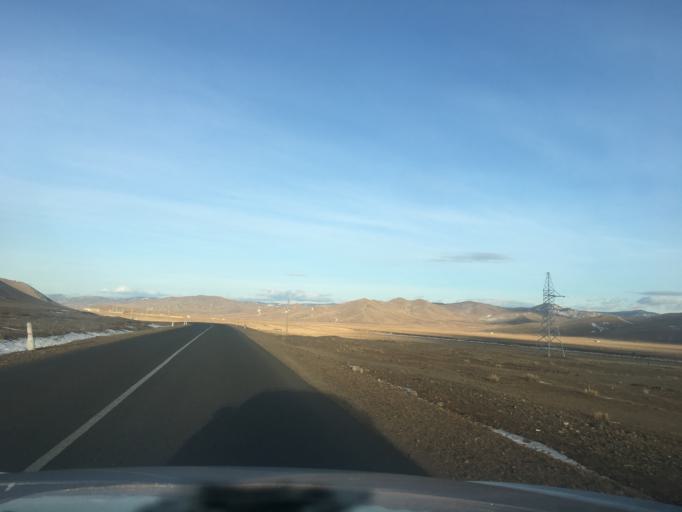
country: MN
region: Central Aimak
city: Mandal
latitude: 48.1086
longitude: 106.6333
